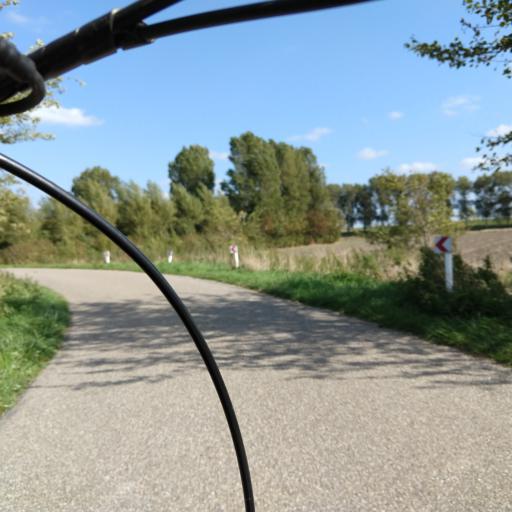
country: NL
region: Zeeland
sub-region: Gemeente Goes
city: Goes
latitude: 51.5576
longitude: 3.8755
